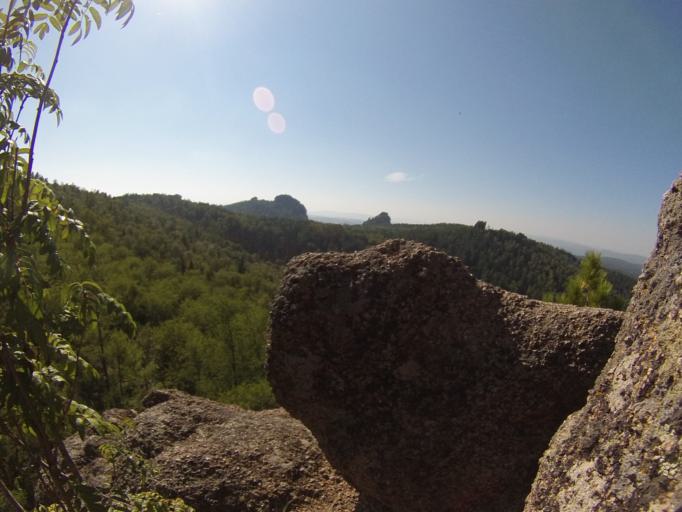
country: RU
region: Krasnoyarskiy
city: Krasnoyarsk
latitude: 55.9149
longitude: 92.7532
